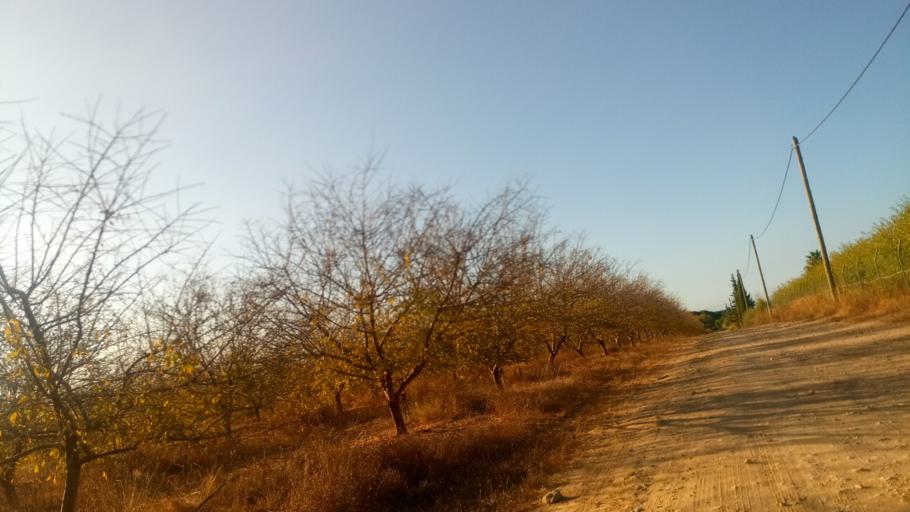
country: PT
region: Faro
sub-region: Tavira
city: Tavira
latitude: 37.1468
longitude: -7.5839
